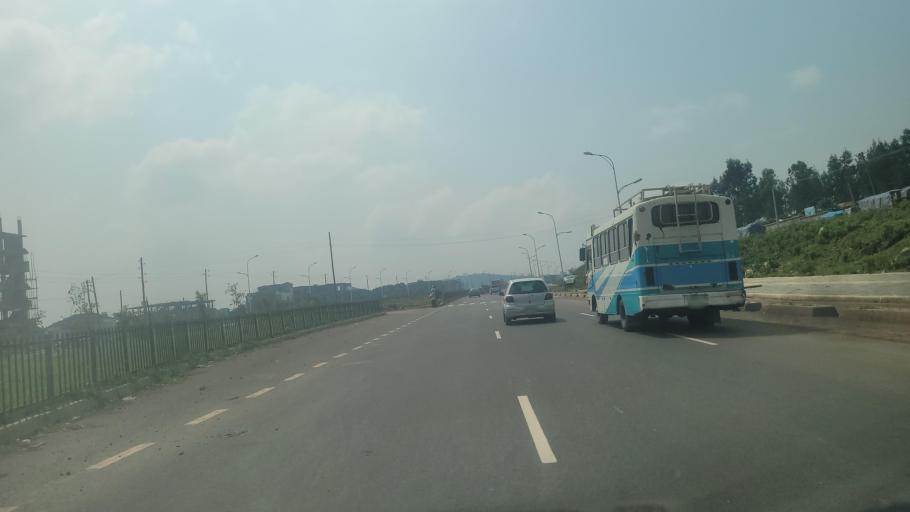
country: ET
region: Adis Abeba
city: Addis Ababa
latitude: 8.9485
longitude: 38.7106
